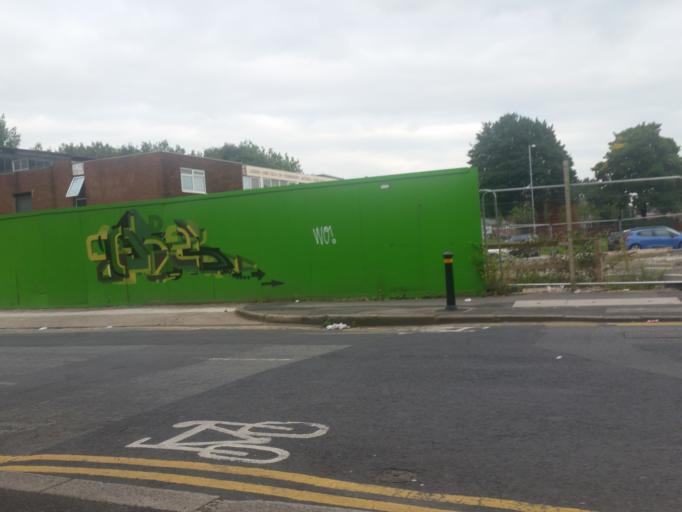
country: GB
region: England
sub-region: Manchester
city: Hulme
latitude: 53.4713
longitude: -2.2634
